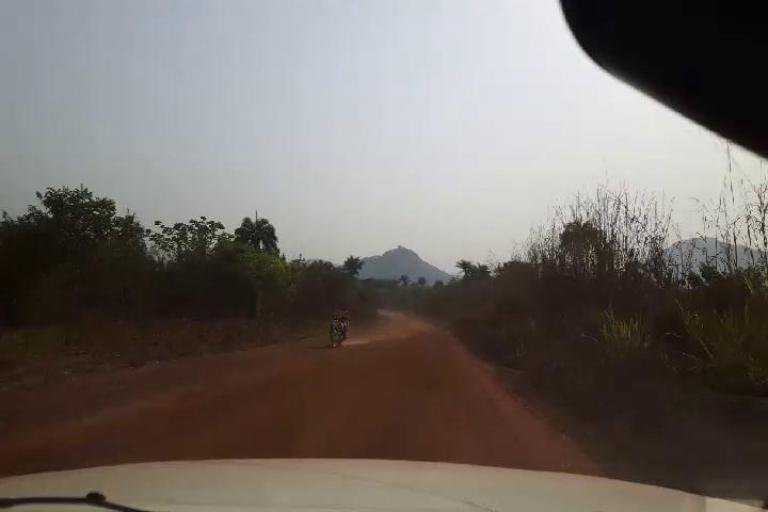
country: SL
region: Northern Province
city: Masingbi
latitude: 8.8465
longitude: -11.8308
